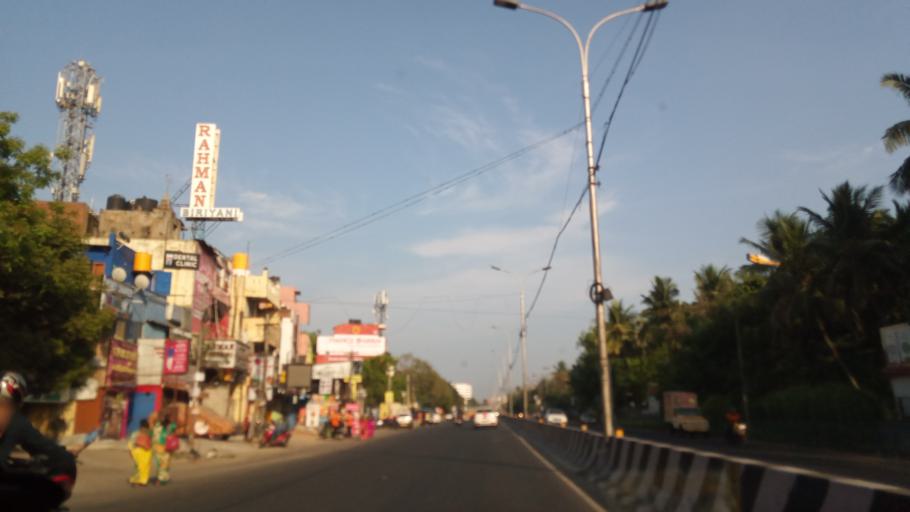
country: IN
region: Tamil Nadu
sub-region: Kancheepuram
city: Manappakkam
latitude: 13.0257
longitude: 80.1753
